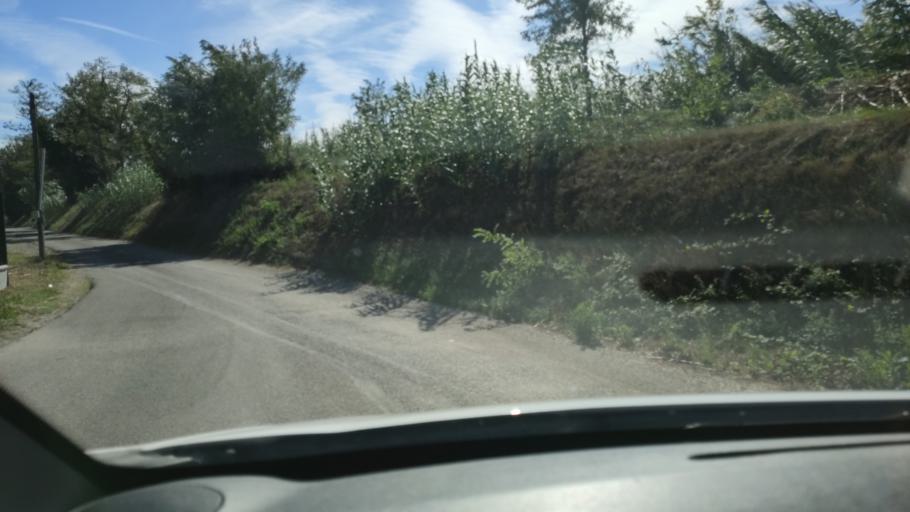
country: FR
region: Provence-Alpes-Cote d'Azur
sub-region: Departement du Vaucluse
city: Morieres-les-Avignon
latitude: 43.9524
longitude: 4.8849
